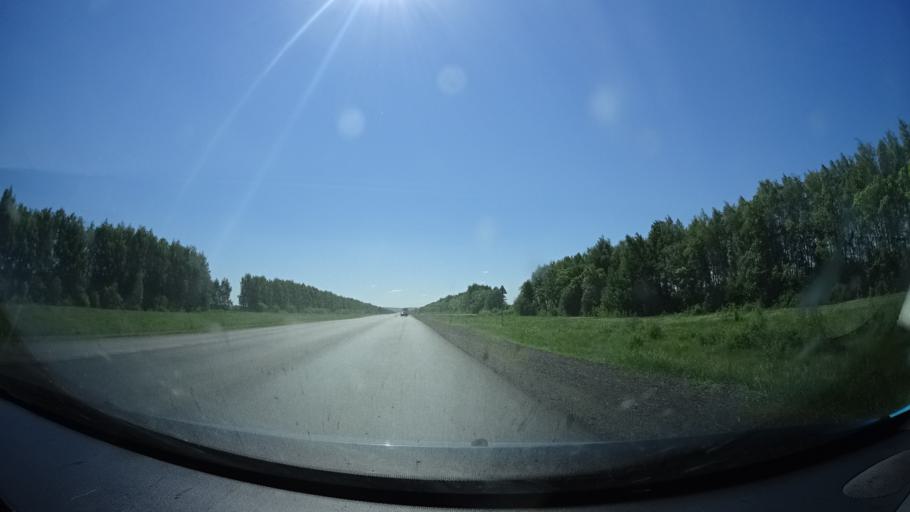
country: RU
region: Bashkortostan
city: Birsk
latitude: 55.2420
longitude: 55.7674
